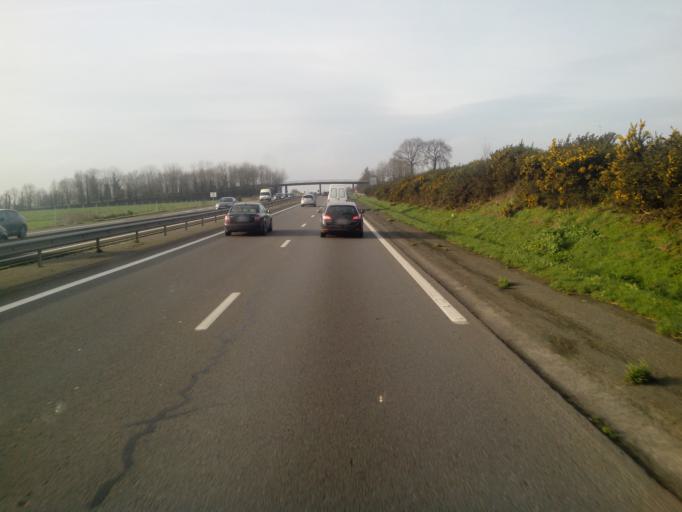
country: FR
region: Brittany
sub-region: Departement d'Ille-et-Vilaine
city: Breteil
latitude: 48.1655
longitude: -1.8672
